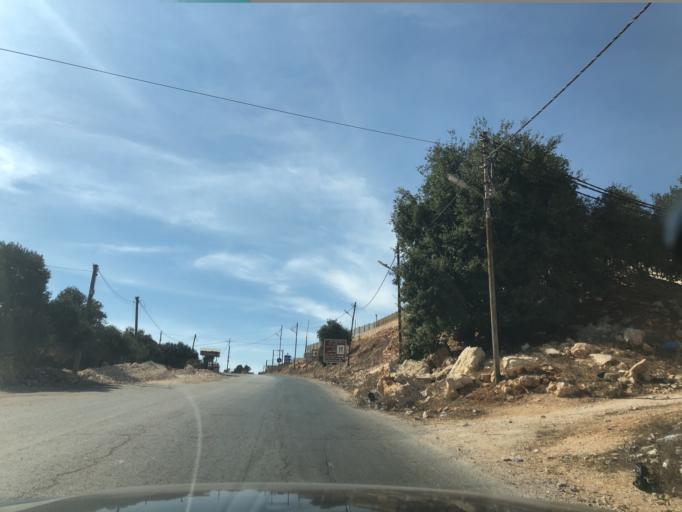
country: JO
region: Ajlun
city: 'Ajlun
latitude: 32.3280
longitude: 35.7285
